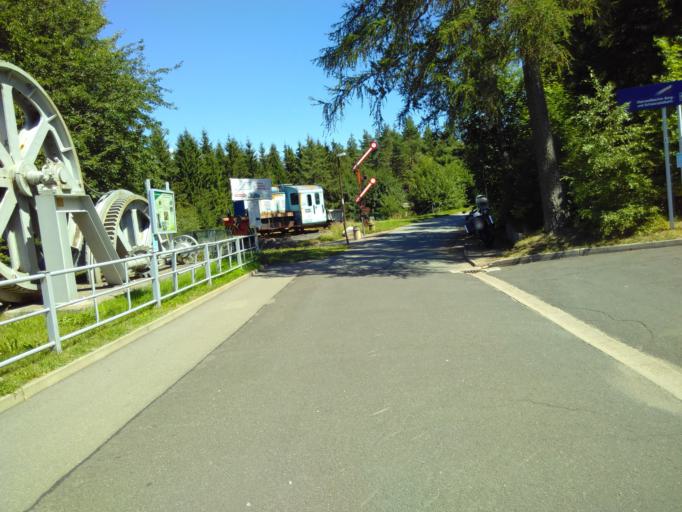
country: DE
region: Thuringia
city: Oberweissbach
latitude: 50.5919
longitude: 11.1330
